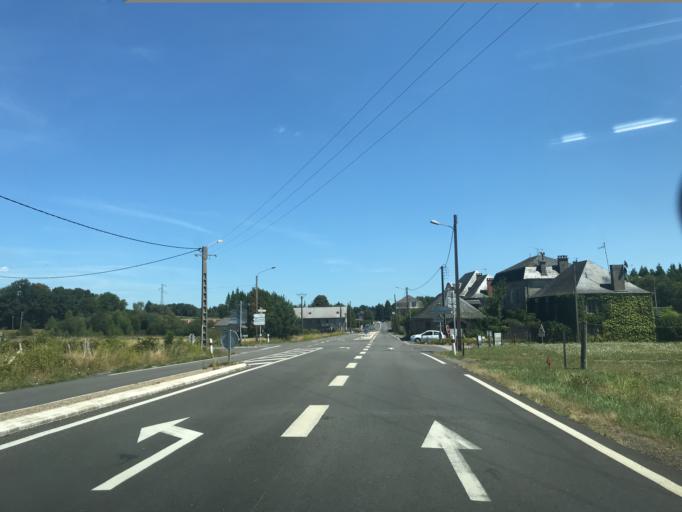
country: FR
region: Limousin
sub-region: Departement de la Correze
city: Correze
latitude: 45.3409
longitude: 1.9295
